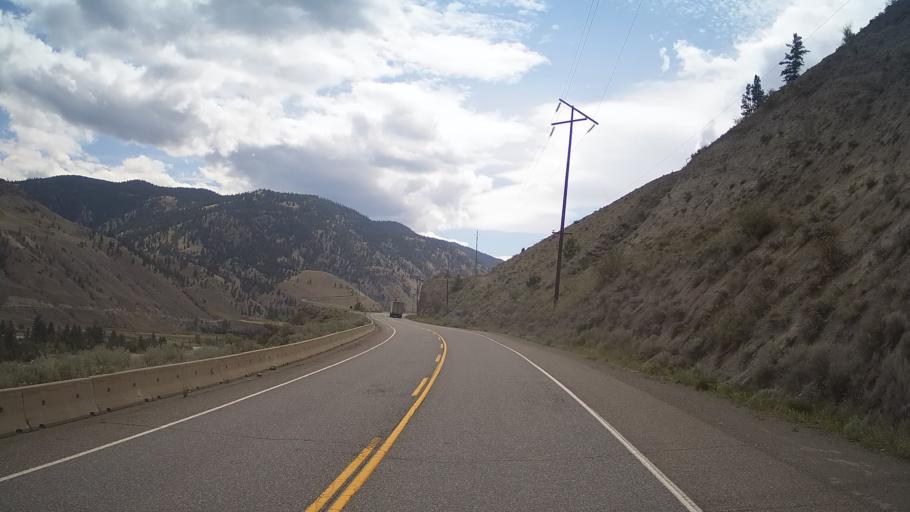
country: CA
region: British Columbia
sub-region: Thompson-Nicola Regional District
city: Ashcroft
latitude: 50.4801
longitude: -121.3018
